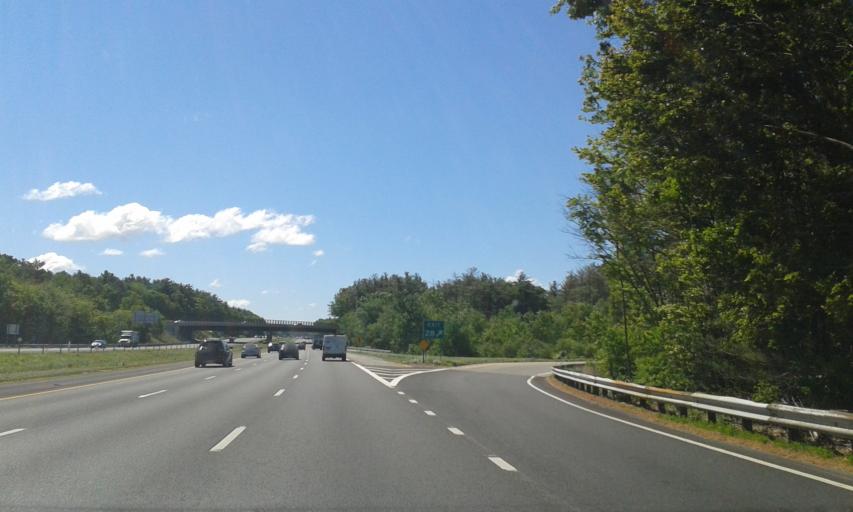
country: US
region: Massachusetts
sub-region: Middlesex County
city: Billerica
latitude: 42.5634
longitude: -71.3001
